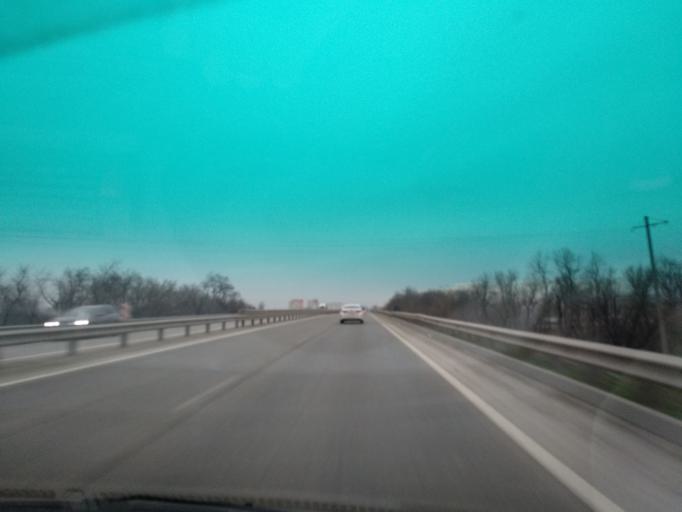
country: RU
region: Krasnodarskiy
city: Pashkovskiy
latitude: 45.0467
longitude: 39.1292
